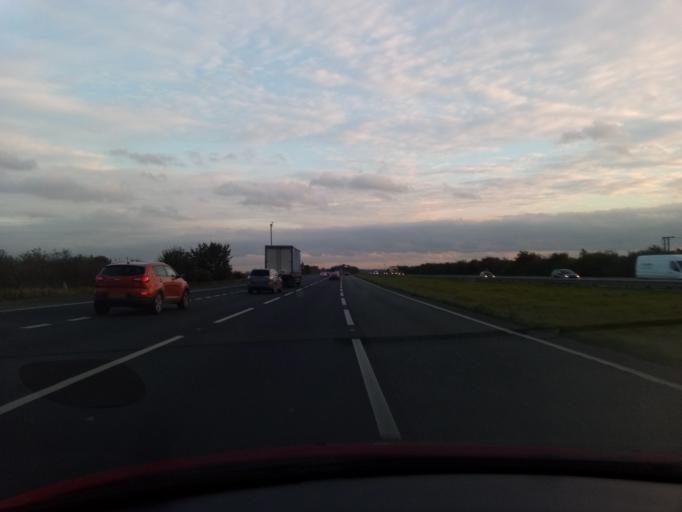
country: GB
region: England
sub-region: City and Borough of Leeds
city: Bramham
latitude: 53.9018
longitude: -1.3728
